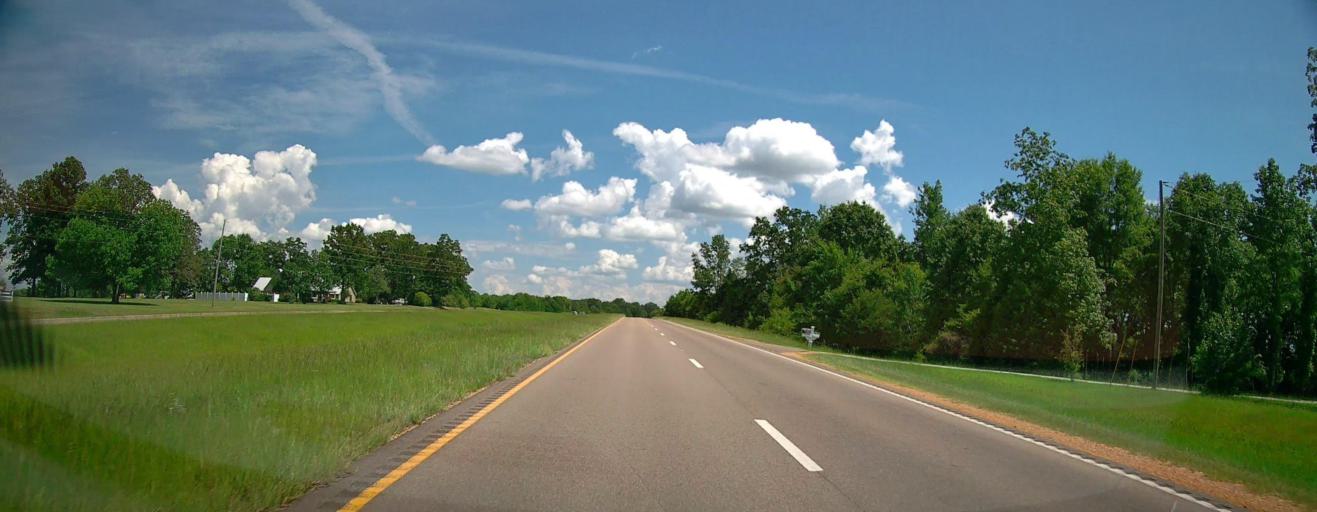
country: US
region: Mississippi
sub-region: Monroe County
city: Amory
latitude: 33.9587
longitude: -88.6101
